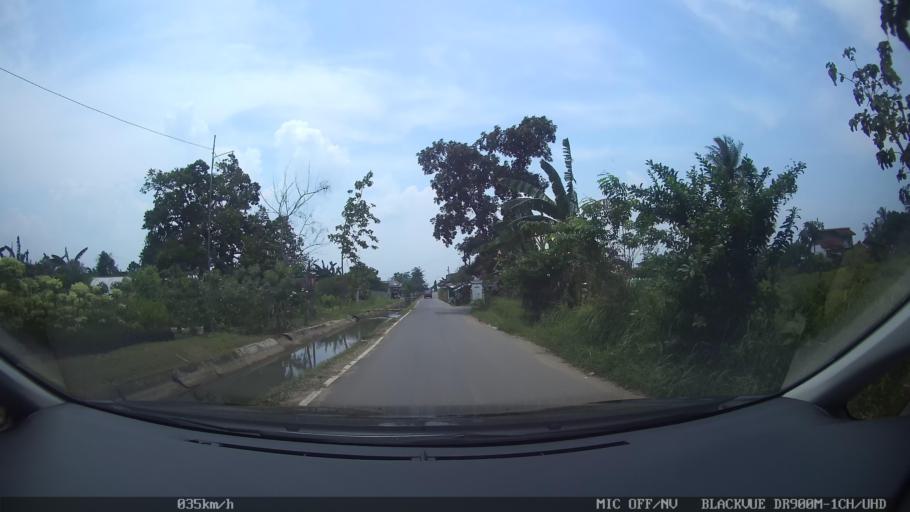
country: ID
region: Lampung
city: Kedaton
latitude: -5.3424
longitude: 105.2455
